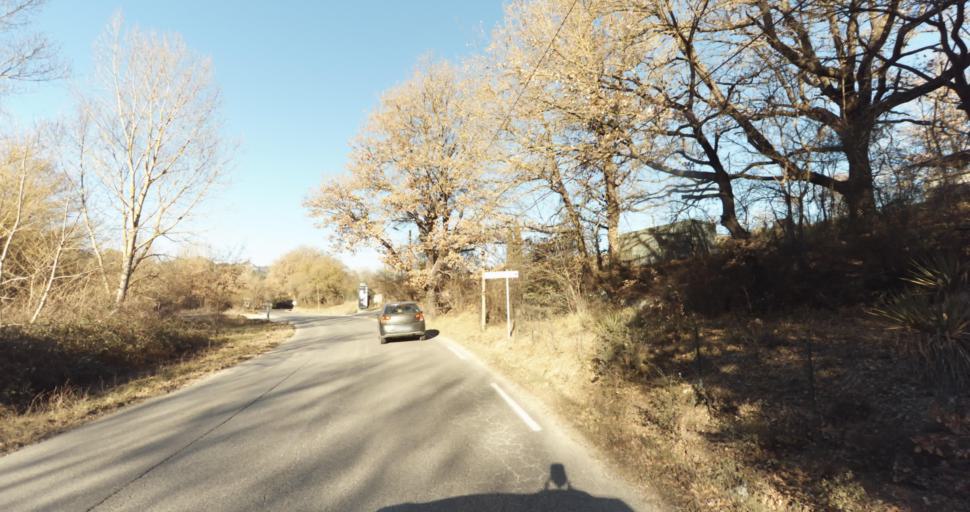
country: FR
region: Provence-Alpes-Cote d'Azur
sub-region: Departement des Bouches-du-Rhone
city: Peypin
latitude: 43.3972
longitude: 5.5721
